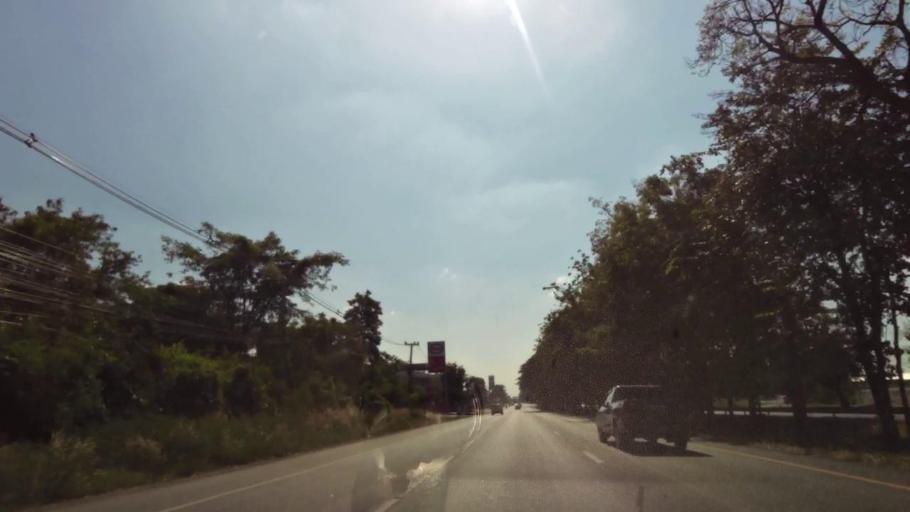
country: TH
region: Nakhon Sawan
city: Nakhon Sawan
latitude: 15.6348
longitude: 100.1302
